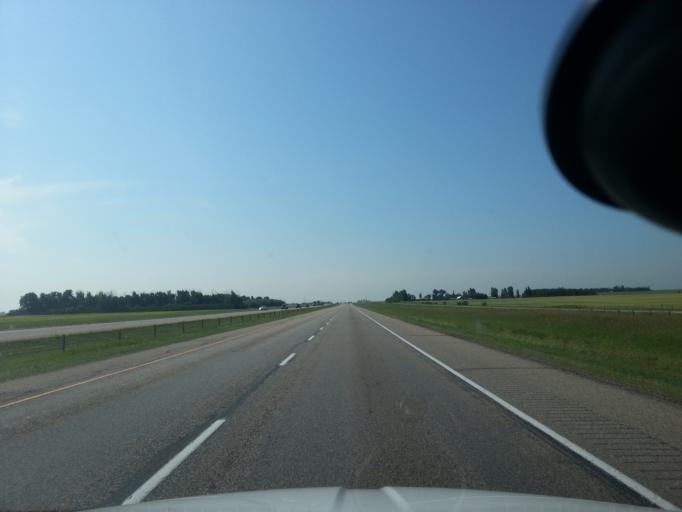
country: CA
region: Alberta
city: Olds
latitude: 51.8390
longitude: -114.0256
